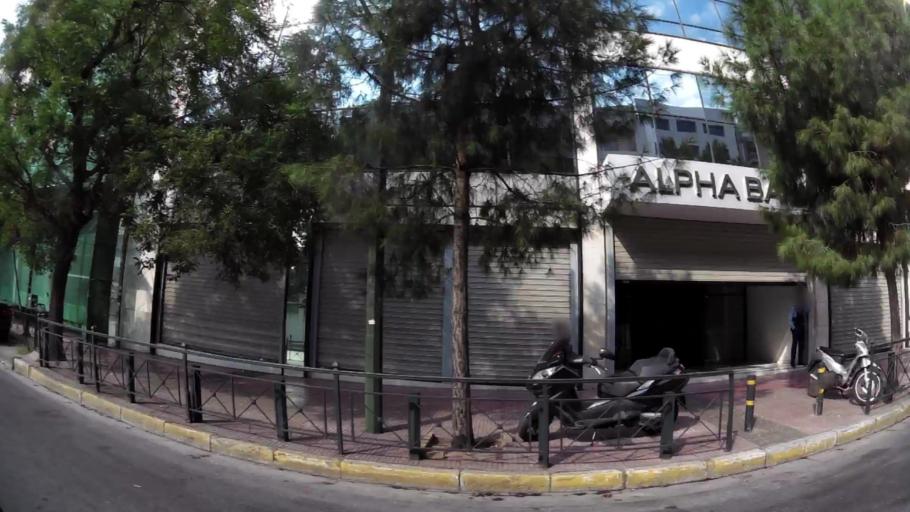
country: GR
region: Attica
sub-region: Nomarchia Athinas
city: Dhafni
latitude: 37.9657
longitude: 23.7281
